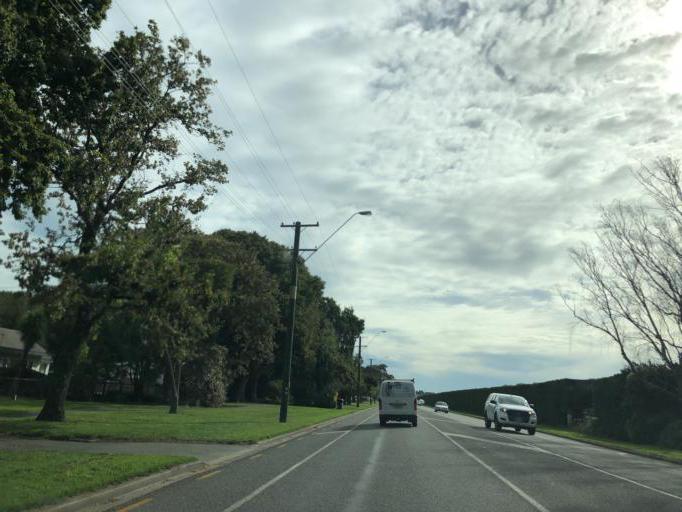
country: NZ
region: Canterbury
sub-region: Selwyn District
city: Lincoln
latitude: -43.6427
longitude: 172.4637
